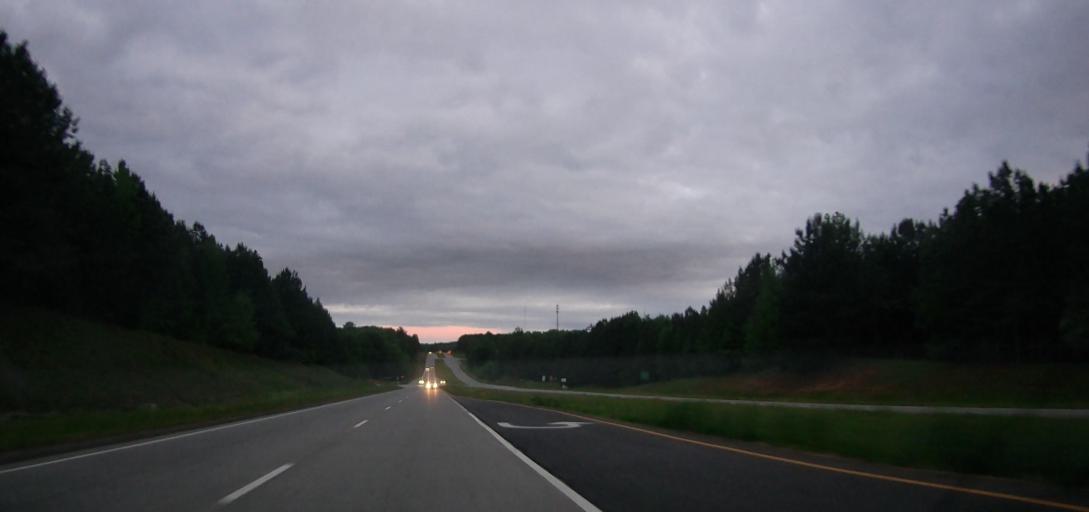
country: US
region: Georgia
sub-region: Jackson County
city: Jefferson
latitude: 34.1147
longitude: -83.5996
